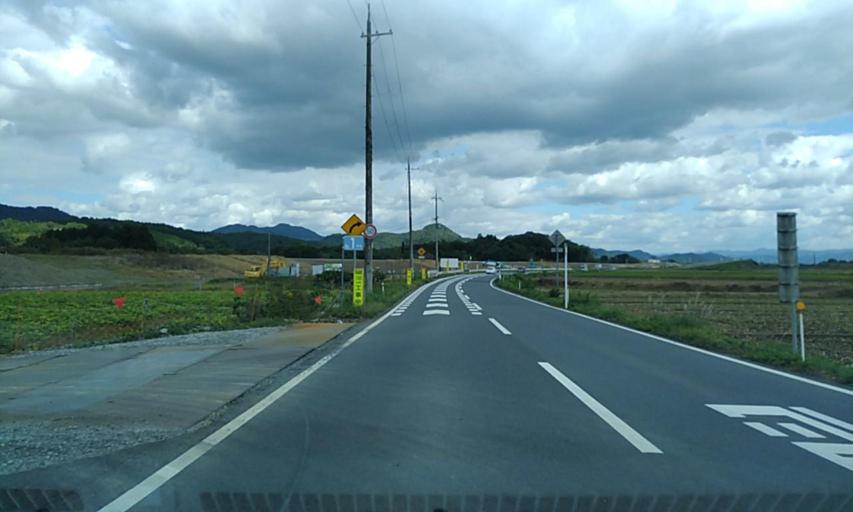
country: JP
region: Kyoto
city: Fukuchiyama
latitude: 35.3023
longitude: 135.1470
